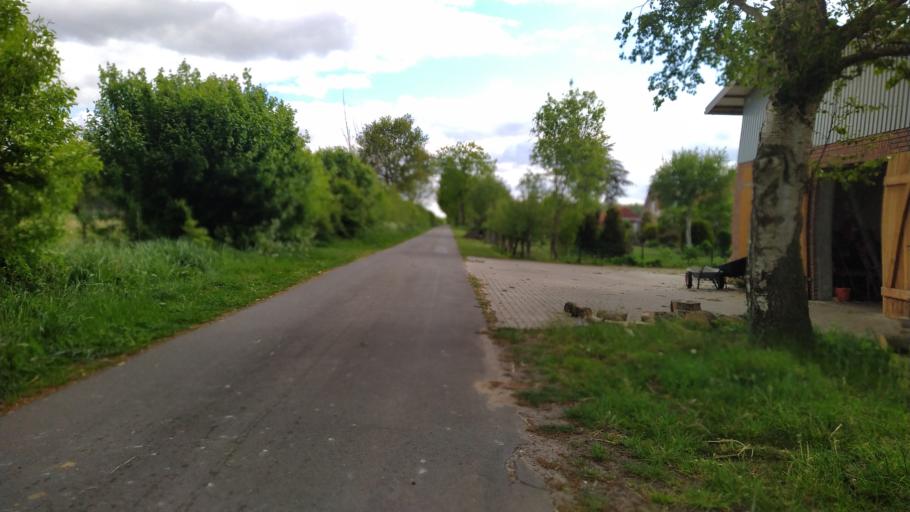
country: DE
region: Lower Saxony
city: Brest
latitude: 53.4472
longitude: 9.3894
